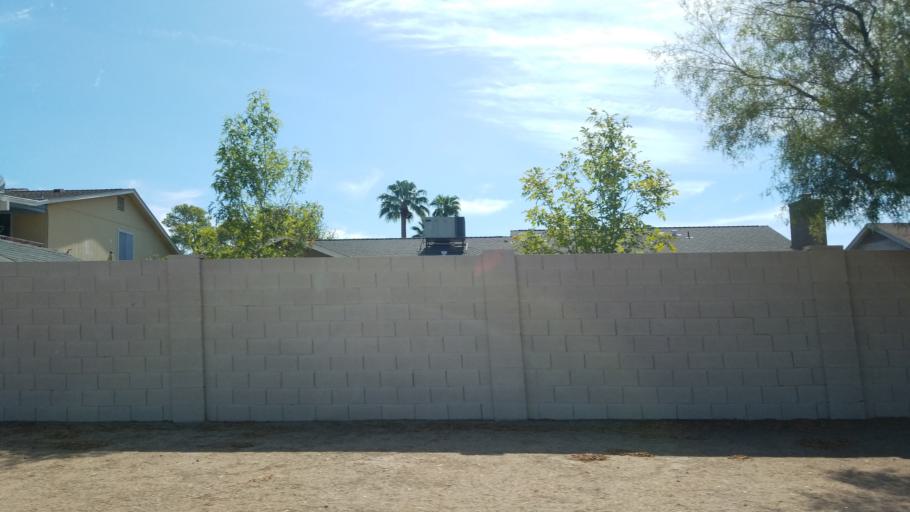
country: US
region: Arizona
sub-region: Maricopa County
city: Peoria
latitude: 33.6523
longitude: -112.1605
